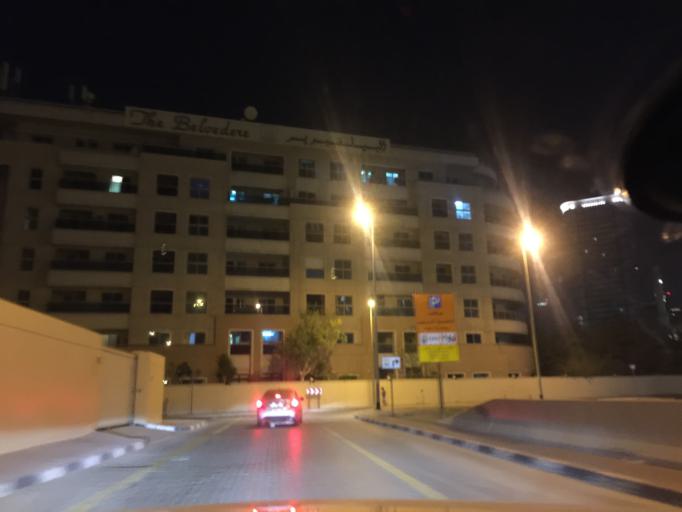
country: AE
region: Dubai
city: Dubai
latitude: 25.0673
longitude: 55.1307
